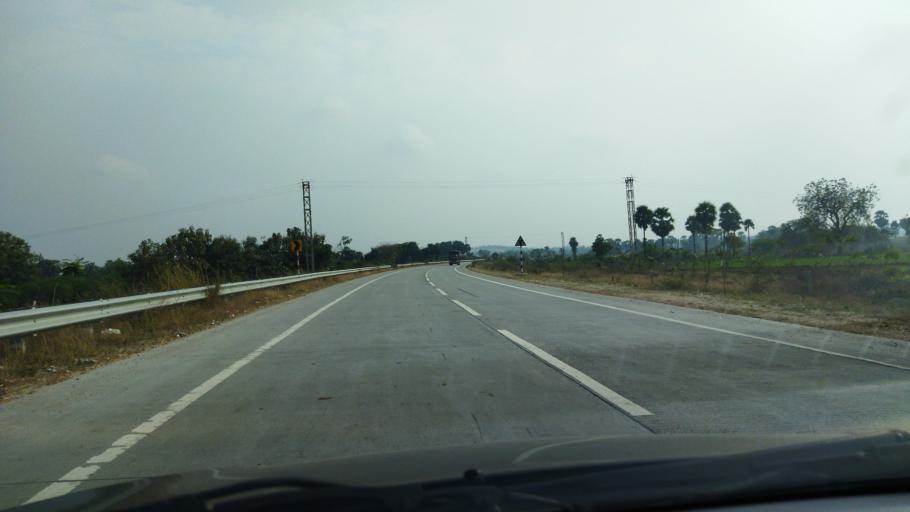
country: IN
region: Telangana
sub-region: Nalgonda
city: Nalgonda
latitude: 17.1751
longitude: 79.3978
